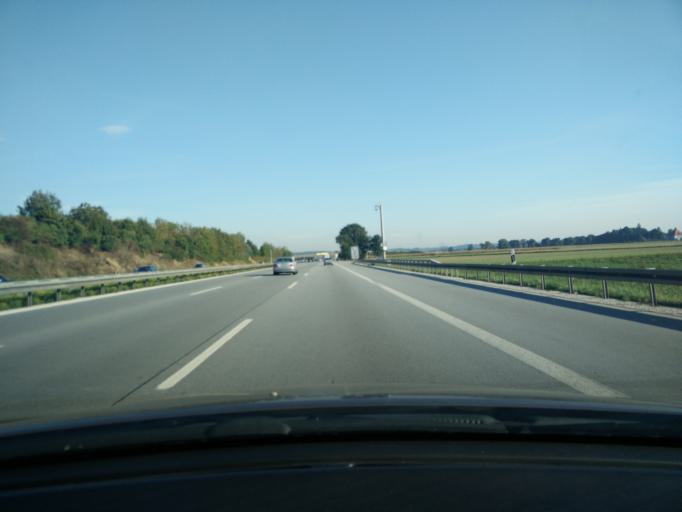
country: DE
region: Bavaria
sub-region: Upper Bavaria
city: Kranzberg
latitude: 48.4080
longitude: 11.5898
